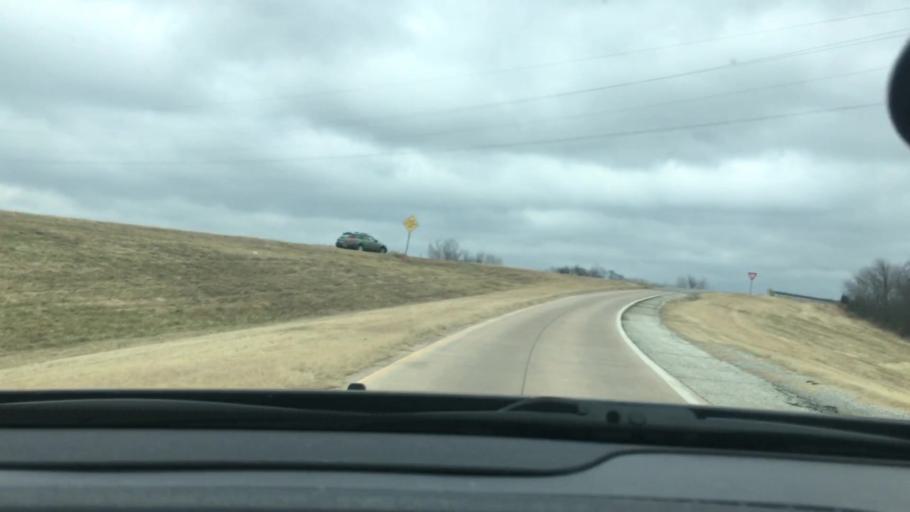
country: US
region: Oklahoma
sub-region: Bryan County
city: Durant
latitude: 34.0378
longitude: -96.3743
